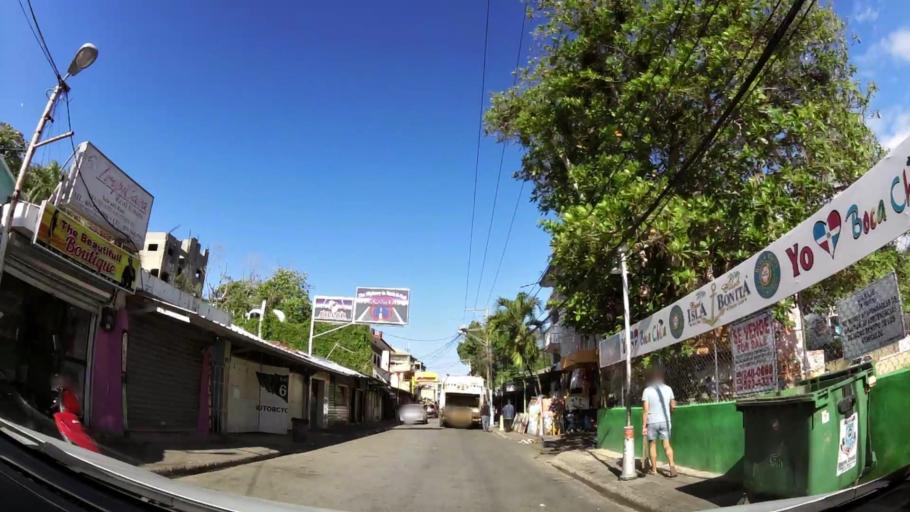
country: DO
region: Santo Domingo
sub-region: Santo Domingo
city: Boca Chica
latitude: 18.4477
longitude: -69.6077
